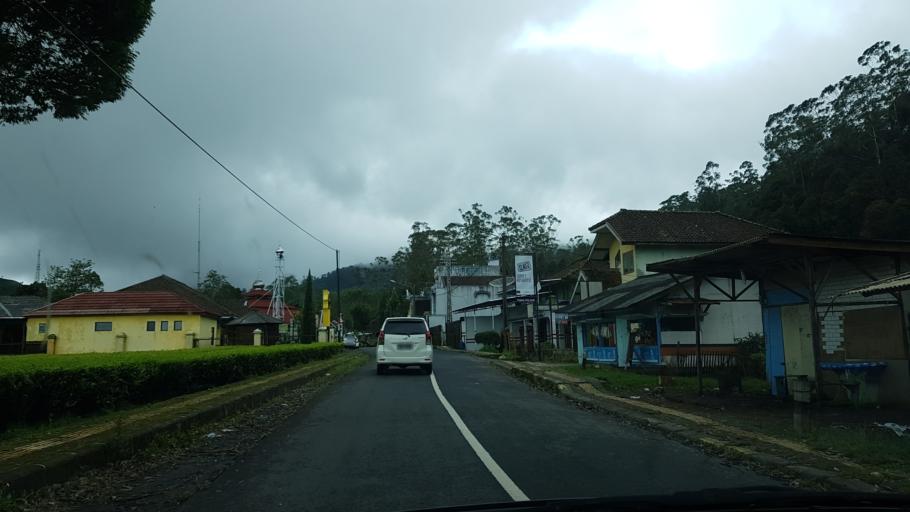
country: ID
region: West Java
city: Banjar
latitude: -7.1544
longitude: 107.3705
